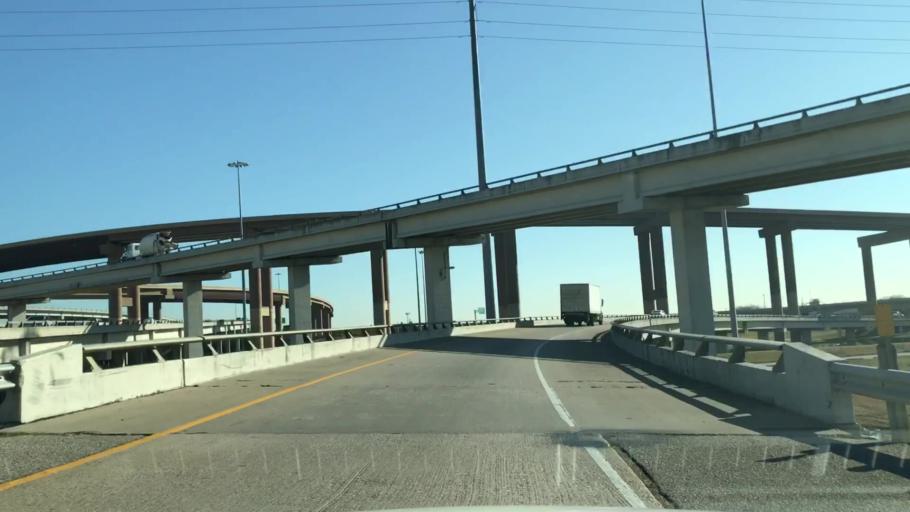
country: US
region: Texas
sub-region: Dallas County
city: Farmers Branch
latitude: 32.9074
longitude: -96.9009
